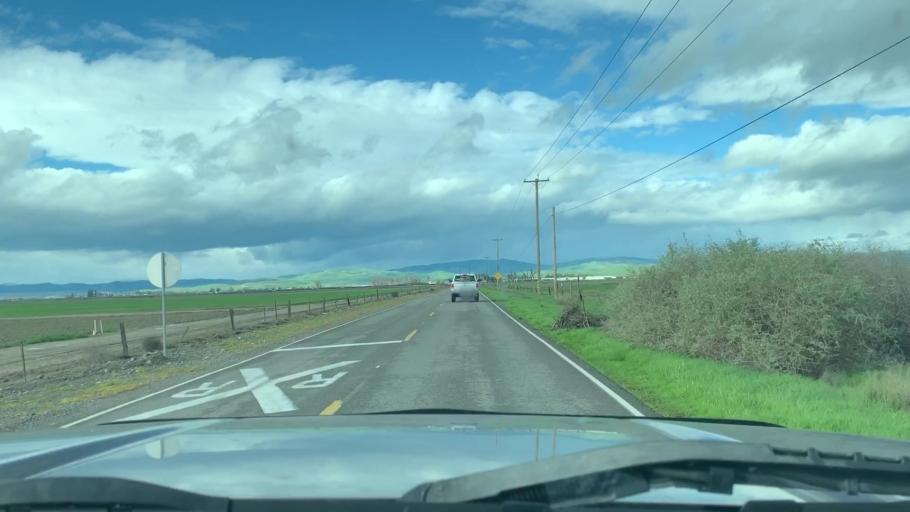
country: US
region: California
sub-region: Merced County
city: Los Banos
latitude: 37.1224
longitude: -120.9487
